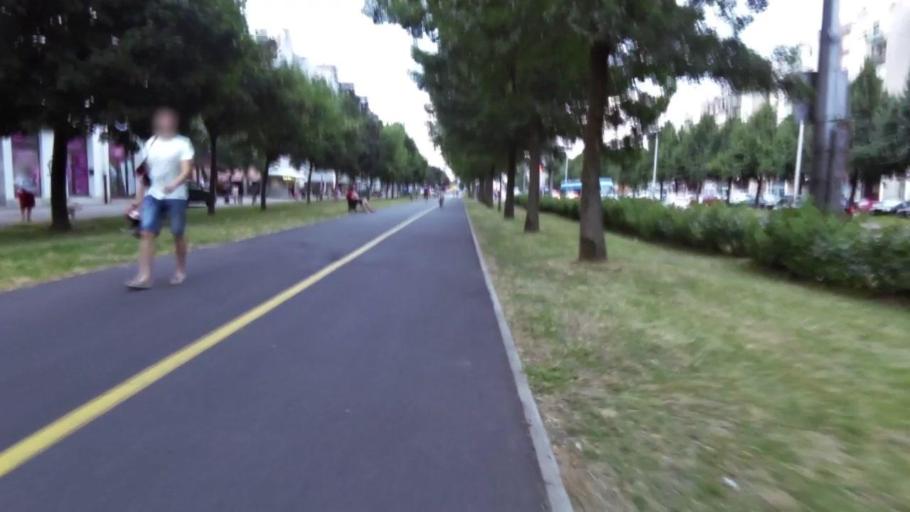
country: HR
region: Grad Zagreb
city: Dubrava
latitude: 45.8286
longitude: 16.0716
